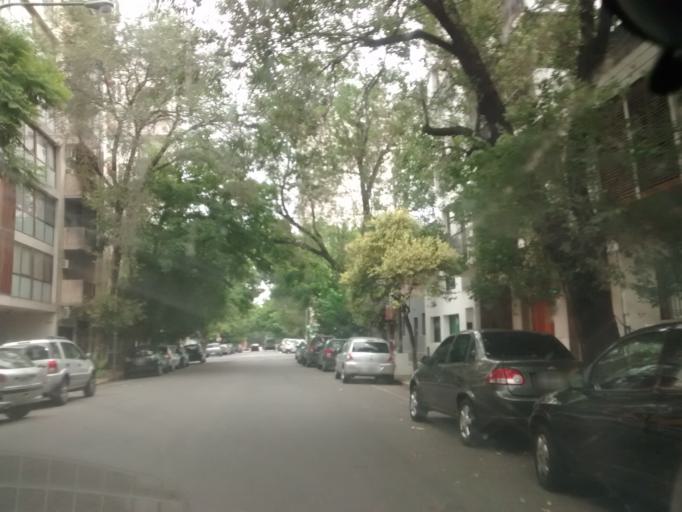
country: AR
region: Buenos Aires
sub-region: Partido de La Plata
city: La Plata
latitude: -34.9098
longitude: -57.9451
